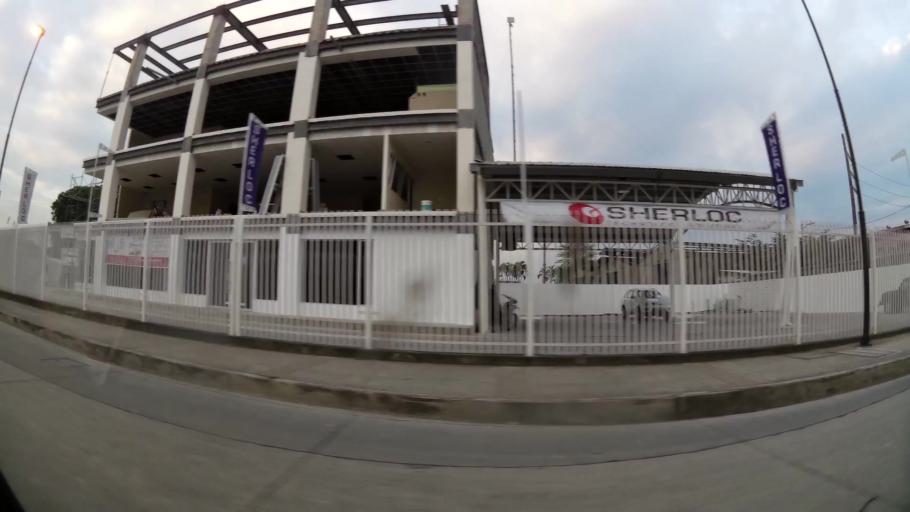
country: EC
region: Guayas
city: Eloy Alfaro
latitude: -2.1721
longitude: -79.8794
